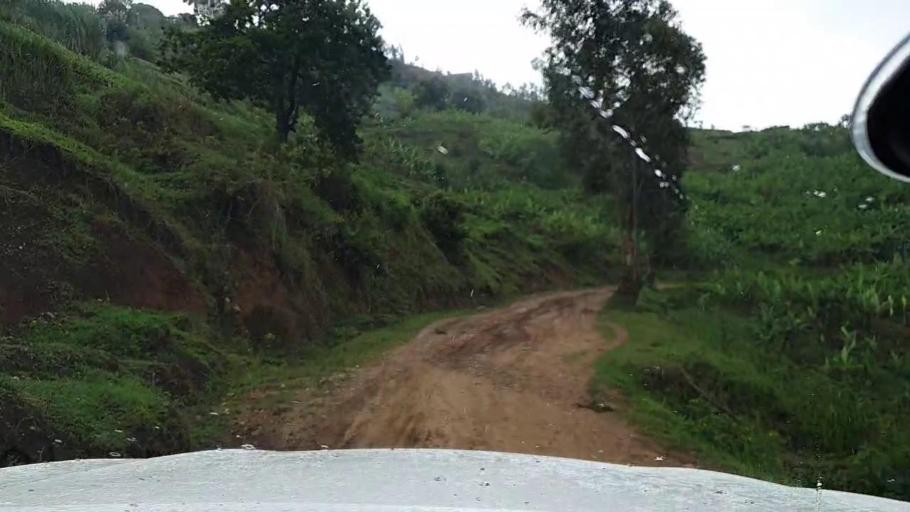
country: RW
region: Western Province
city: Kibuye
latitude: -2.0783
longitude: 29.4472
